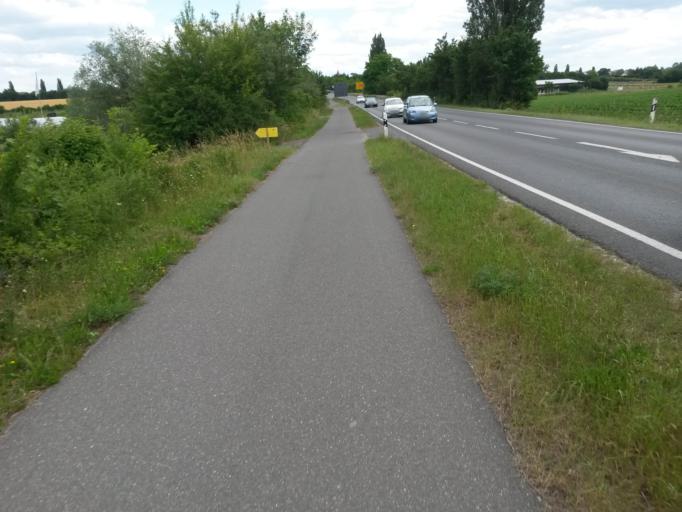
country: DE
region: Bavaria
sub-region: Regierungsbezirk Mittelfranken
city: Seukendorf
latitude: 49.4803
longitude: 10.8702
